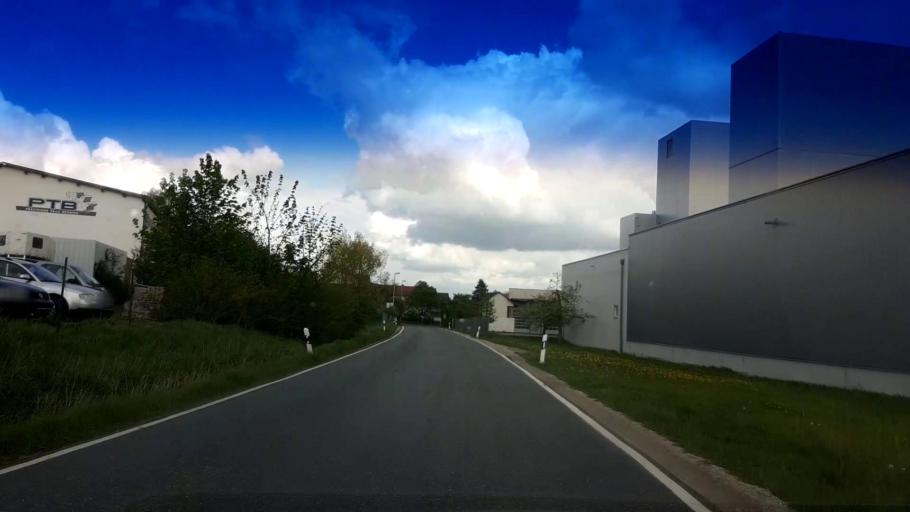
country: DE
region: Bavaria
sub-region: Upper Franconia
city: Pommersfelden
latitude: 49.7795
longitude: 10.8351
